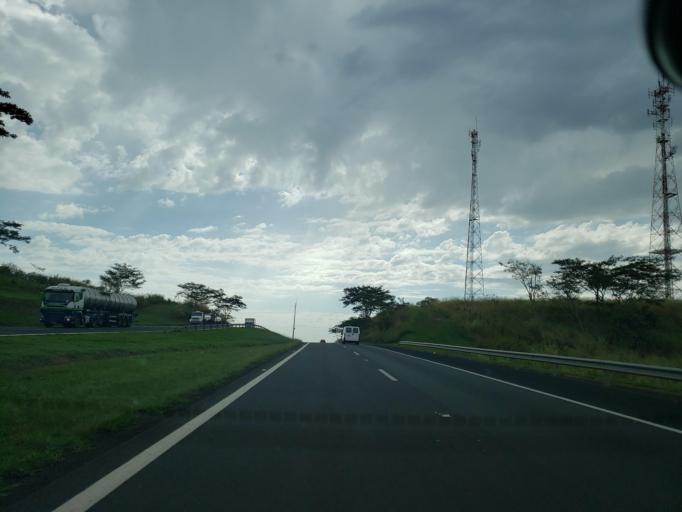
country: BR
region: Sao Paulo
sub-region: Cafelandia
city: Cafelandia
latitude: -21.7604
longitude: -49.6749
